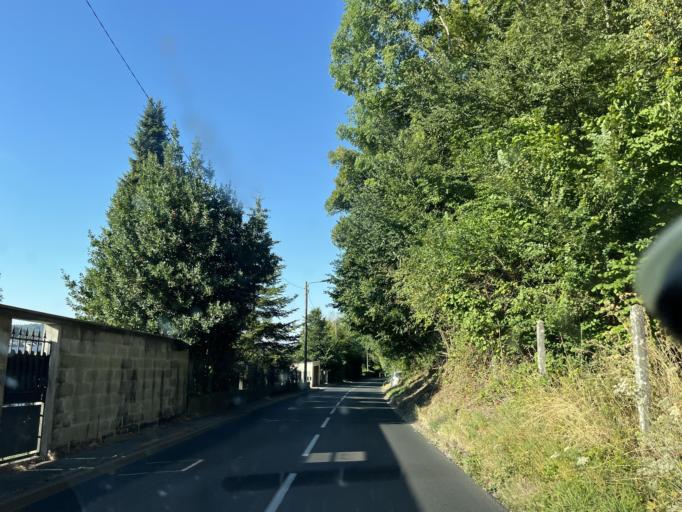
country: FR
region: Haute-Normandie
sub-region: Departement de la Seine-Maritime
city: Lillebonne
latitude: 49.5281
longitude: 0.5433
